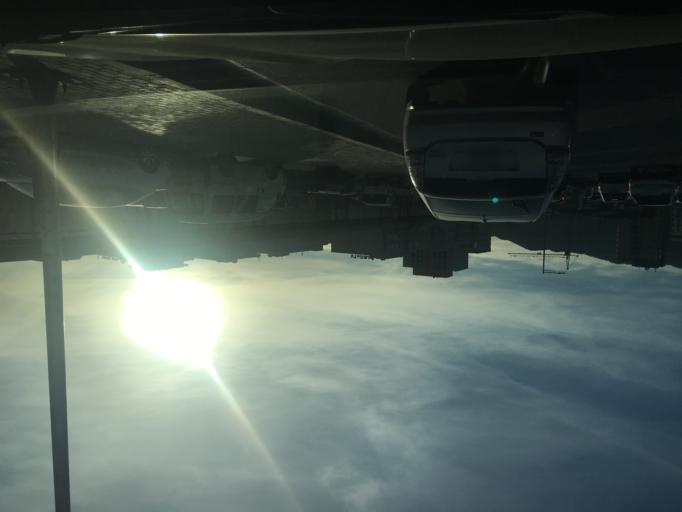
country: MN
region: Ulaanbaatar
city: Ulaanbaatar
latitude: 47.9047
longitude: 106.8934
